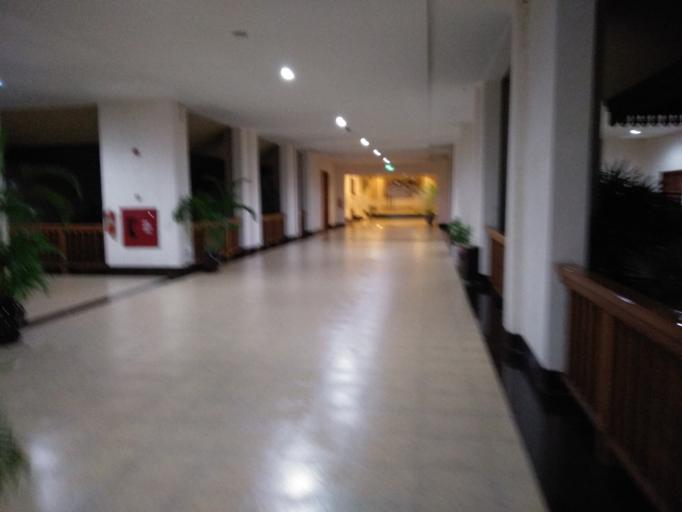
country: MM
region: Mandalay
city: Nay Pyi Taw
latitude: 19.7000
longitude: 96.0844
